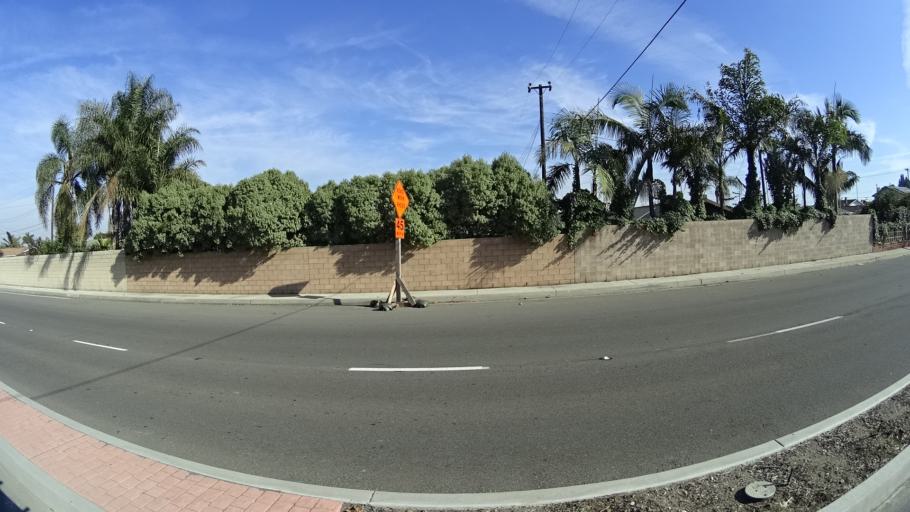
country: US
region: California
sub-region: Orange County
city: Westminster
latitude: 33.7676
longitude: -118.0427
